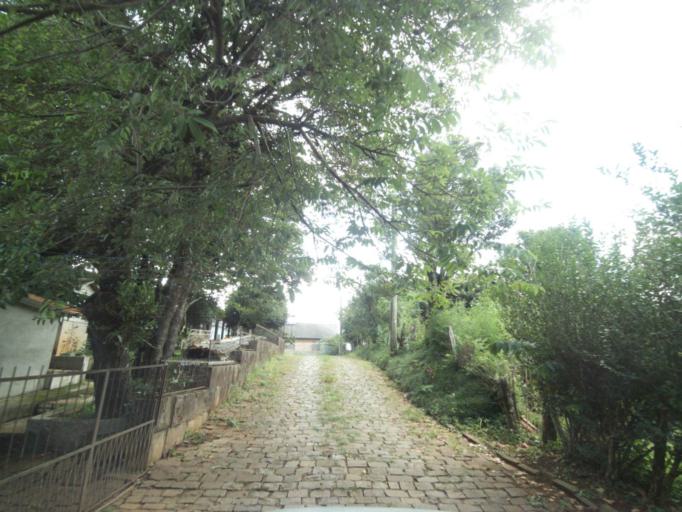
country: BR
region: Rio Grande do Sul
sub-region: Lagoa Vermelha
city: Lagoa Vermelha
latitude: -28.2091
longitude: -51.5366
